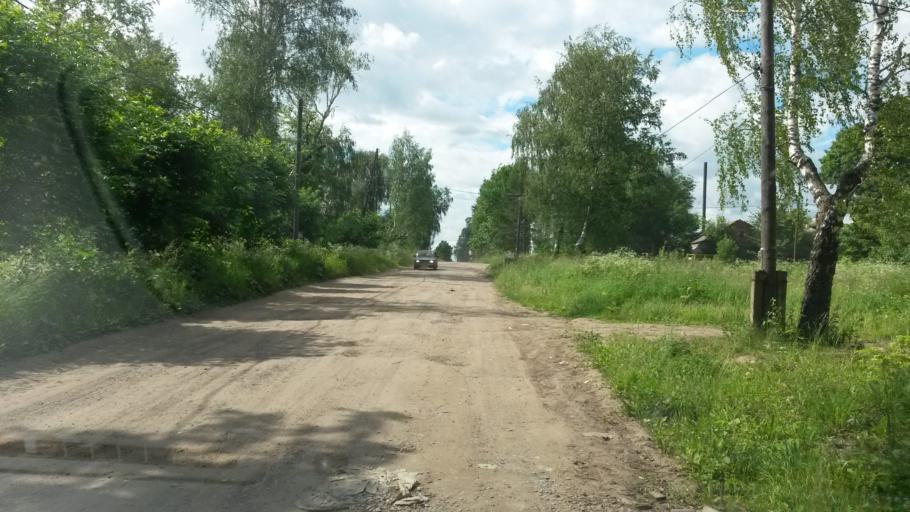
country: RU
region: Jaroslavl
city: Tutayev
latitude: 57.8867
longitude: 39.5368
